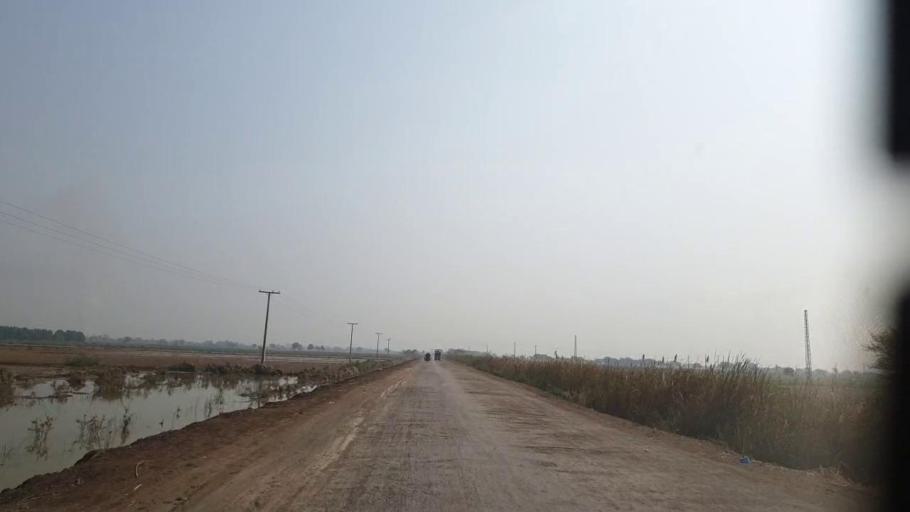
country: PK
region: Sindh
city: Mirpur Khas
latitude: 25.5490
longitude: 69.0643
